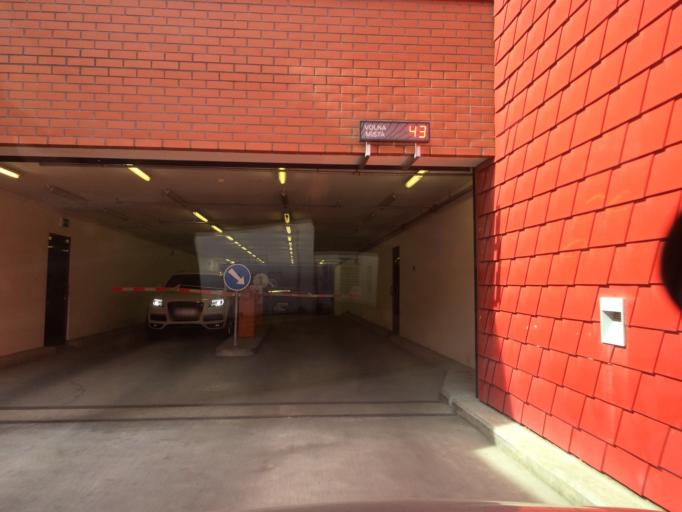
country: CZ
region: Praha
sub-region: Praha 1
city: Mala Strana
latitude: 50.1056
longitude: 14.3898
